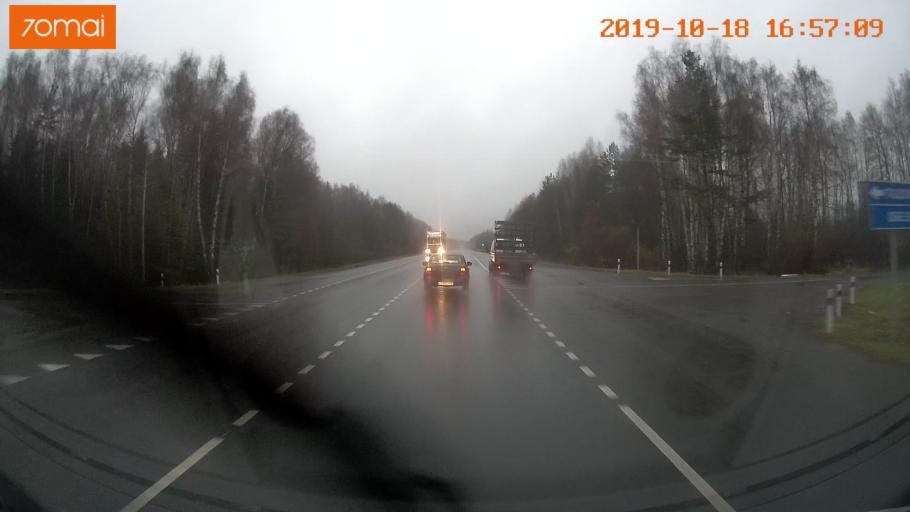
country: RU
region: Ivanovo
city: Novoye Leushino
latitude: 56.6639
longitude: 40.5928
